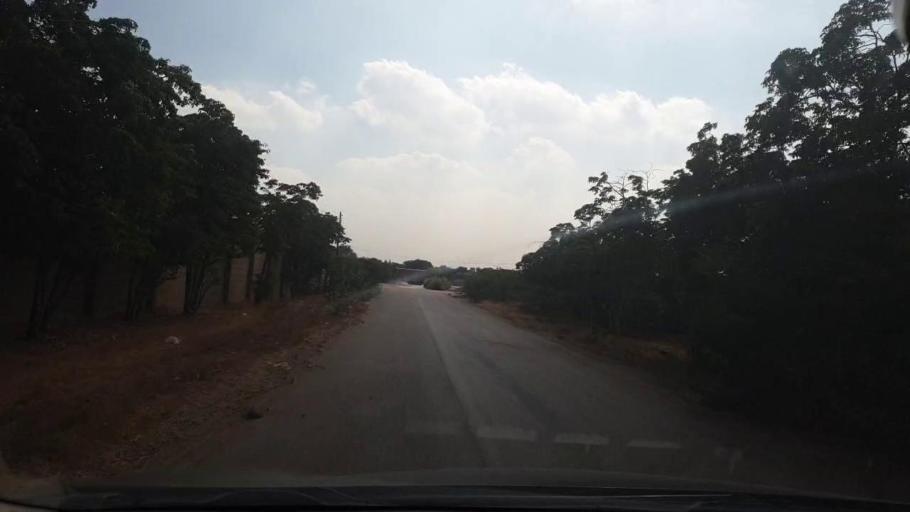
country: PK
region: Sindh
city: Malir Cantonment
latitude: 25.0089
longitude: 67.3556
